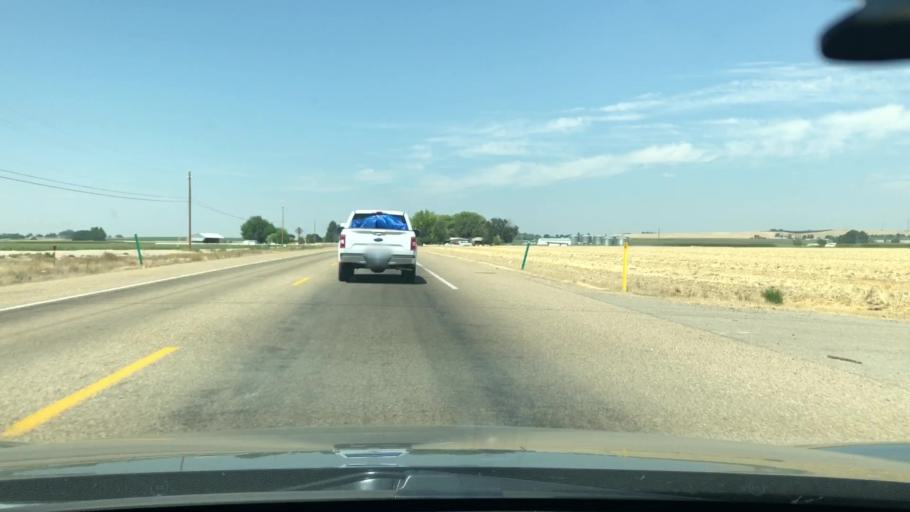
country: US
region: Idaho
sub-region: Canyon County
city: Parma
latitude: 43.7959
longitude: -116.9522
